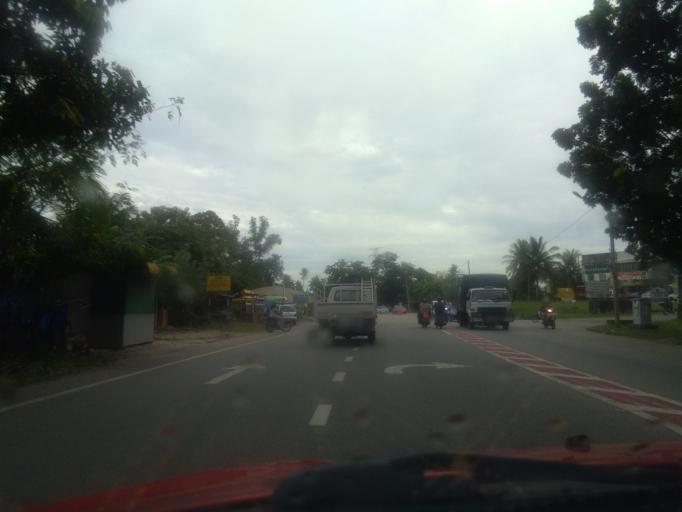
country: MY
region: Kedah
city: Sungai Petani
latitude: 5.6291
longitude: 100.5249
